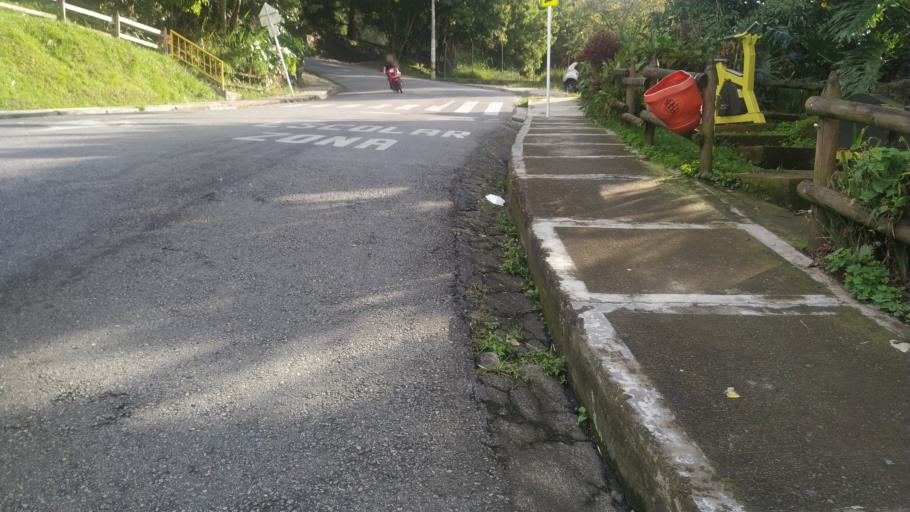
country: CO
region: Antioquia
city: Medellin
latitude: 6.2259
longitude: -75.5425
